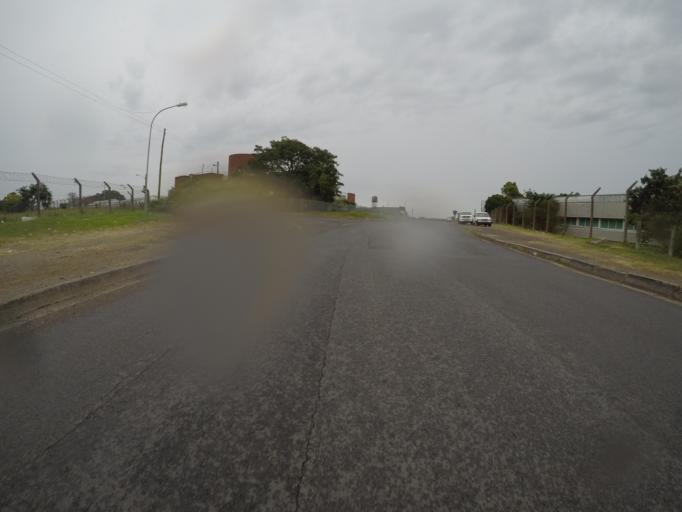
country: ZA
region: Eastern Cape
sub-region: Buffalo City Metropolitan Municipality
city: East London
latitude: -32.9728
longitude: 27.8230
